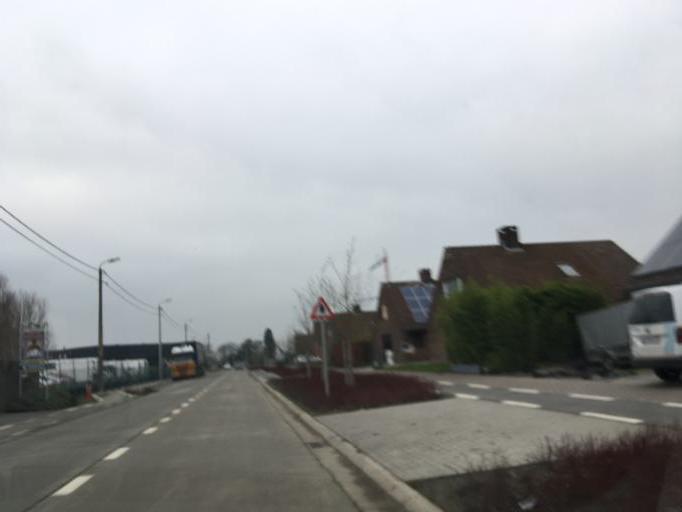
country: BE
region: Flanders
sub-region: Provincie West-Vlaanderen
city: Hooglede
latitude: 50.9959
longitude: 3.1190
